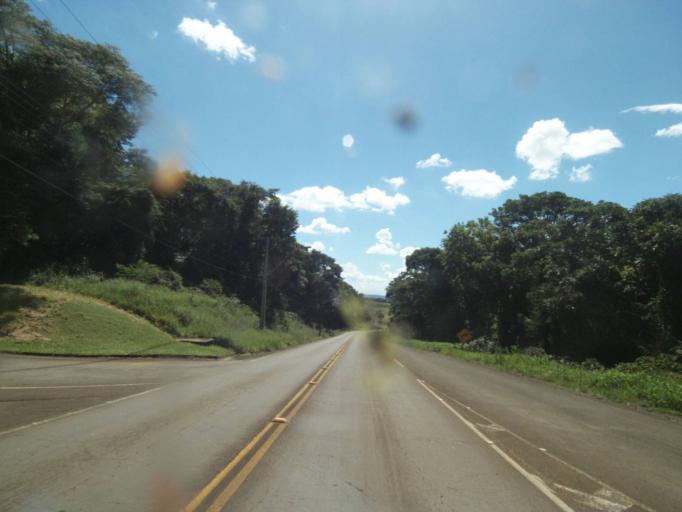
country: BR
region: Parana
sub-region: Chopinzinho
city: Chopinzinho
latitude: -25.7911
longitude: -52.0913
